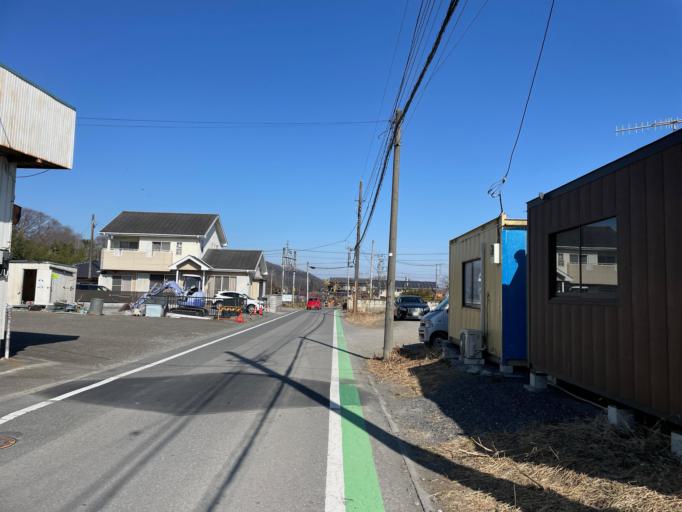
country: JP
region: Saitama
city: Yorii
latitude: 36.1129
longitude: 139.2071
